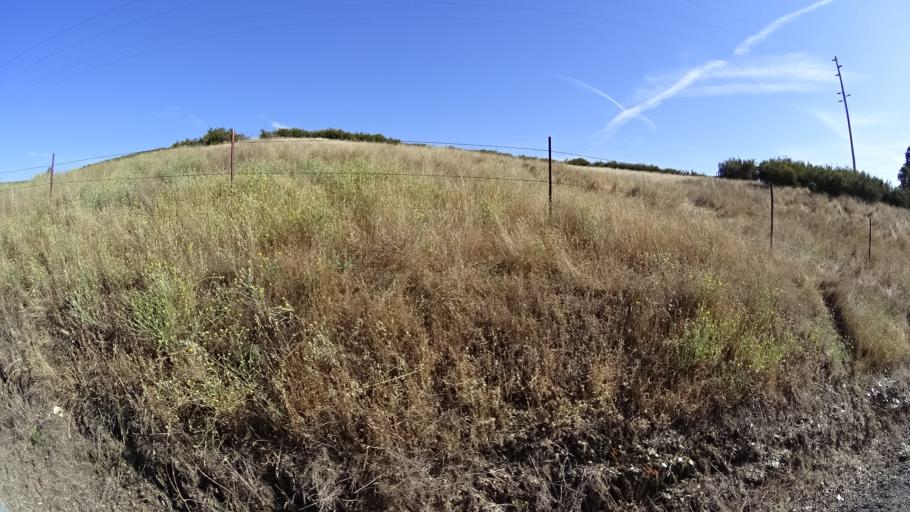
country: US
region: California
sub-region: Calaveras County
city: Valley Springs
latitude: 38.1510
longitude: -120.8191
